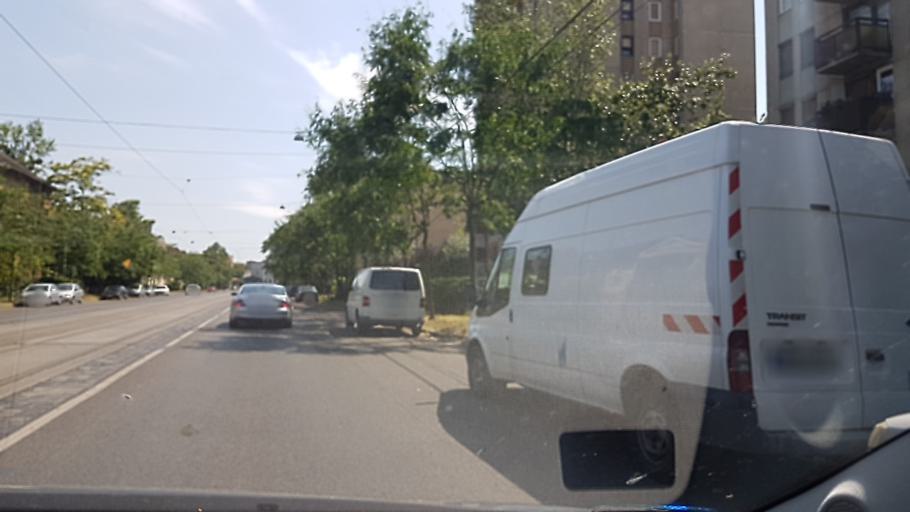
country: HU
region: Budapest
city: Budapest VIII. keruelet
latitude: 47.4842
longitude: 19.0930
